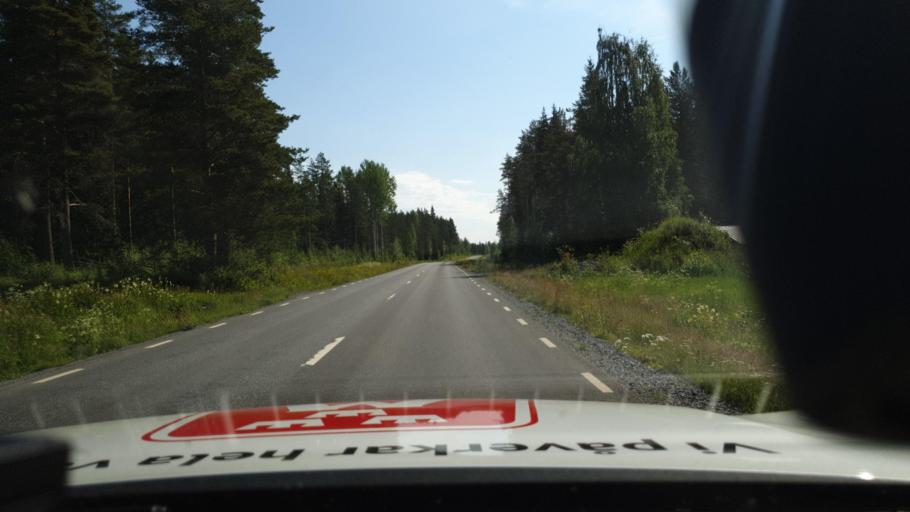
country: SE
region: Norrbotten
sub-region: Lulea Kommun
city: Ranea
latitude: 65.7907
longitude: 22.1277
